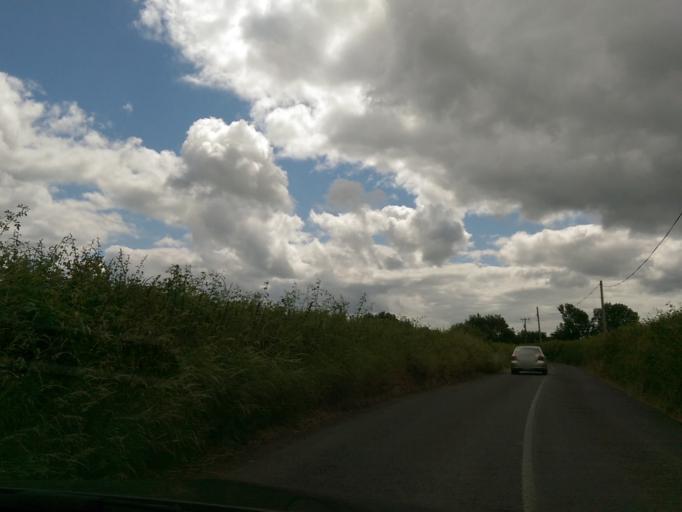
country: IE
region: Munster
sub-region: North Tipperary
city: Nenagh
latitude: 52.8311
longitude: -8.2019
